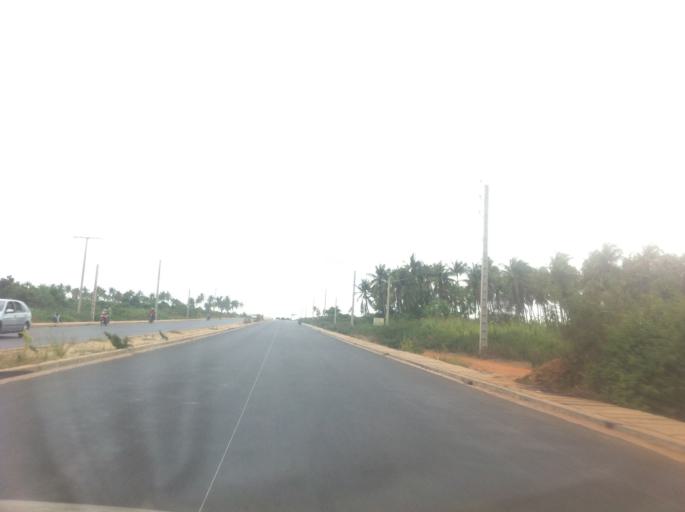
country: BJ
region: Atlantique
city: Ouidah
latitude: 6.3666
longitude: 2.0602
